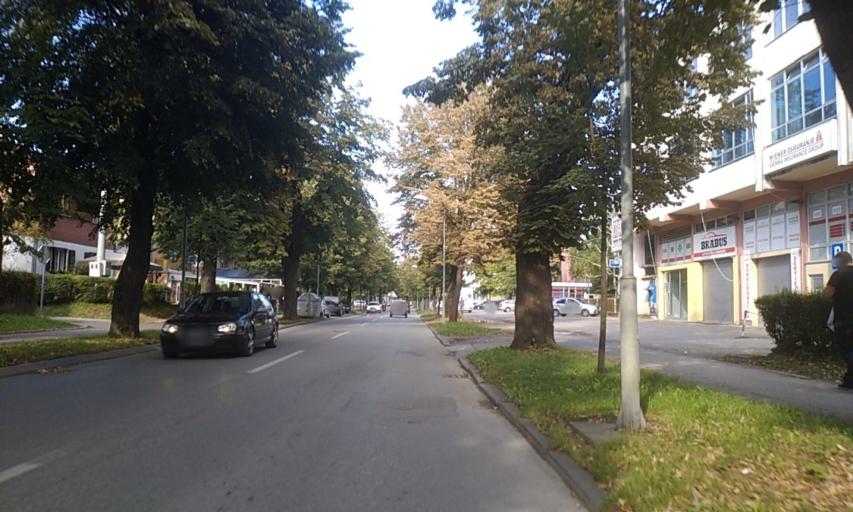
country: BA
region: Republika Srpska
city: Hiseti
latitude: 44.7623
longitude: 17.1821
